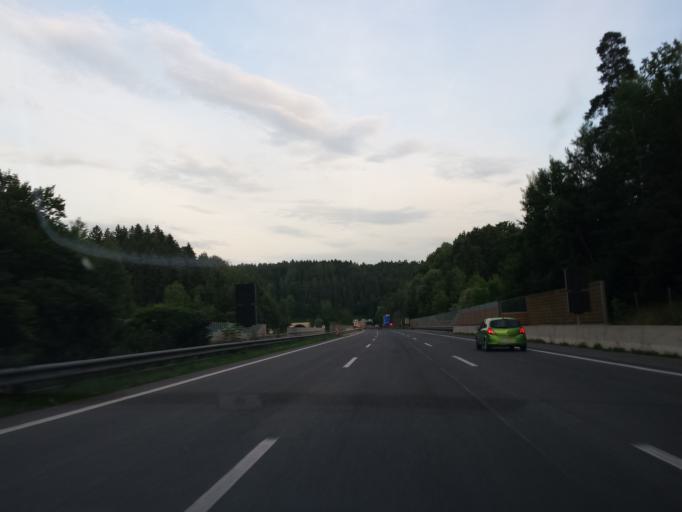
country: AT
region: Styria
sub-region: Politischer Bezirk Graz-Umgebung
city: Gratkorn
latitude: 47.1329
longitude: 15.3578
